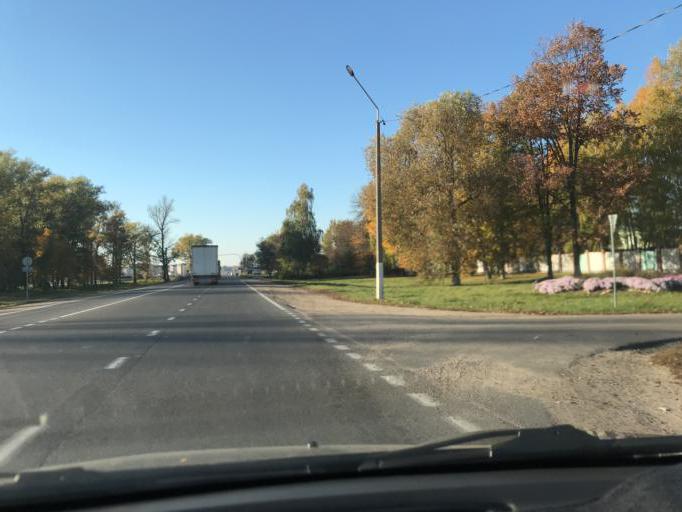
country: BY
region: Minsk
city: Slutsk
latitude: 53.0414
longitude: 27.5824
